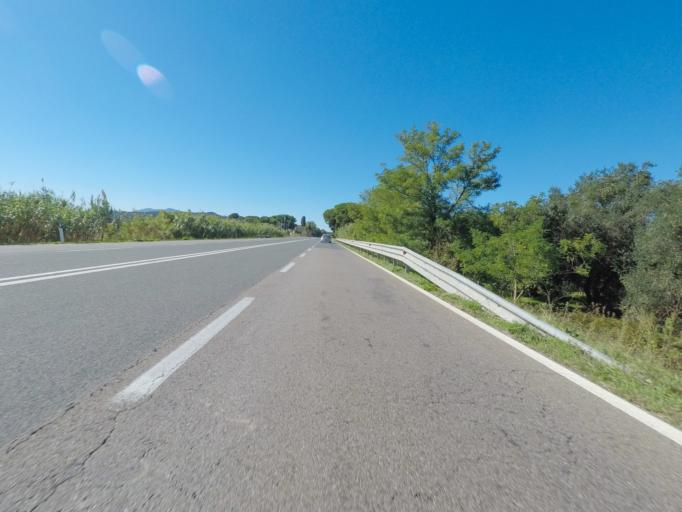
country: IT
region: Tuscany
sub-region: Provincia di Grosseto
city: Orbetello Scalo
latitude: 42.4160
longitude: 11.3160
